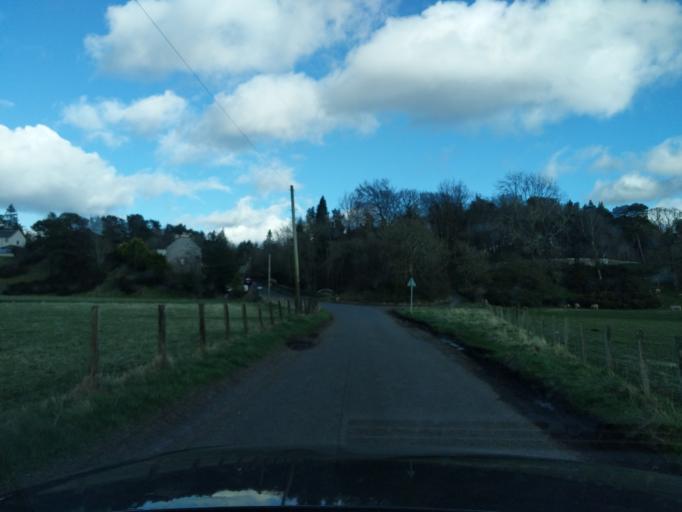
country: GB
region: Scotland
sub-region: Edinburgh
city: Balerno
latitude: 55.8774
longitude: -3.3752
